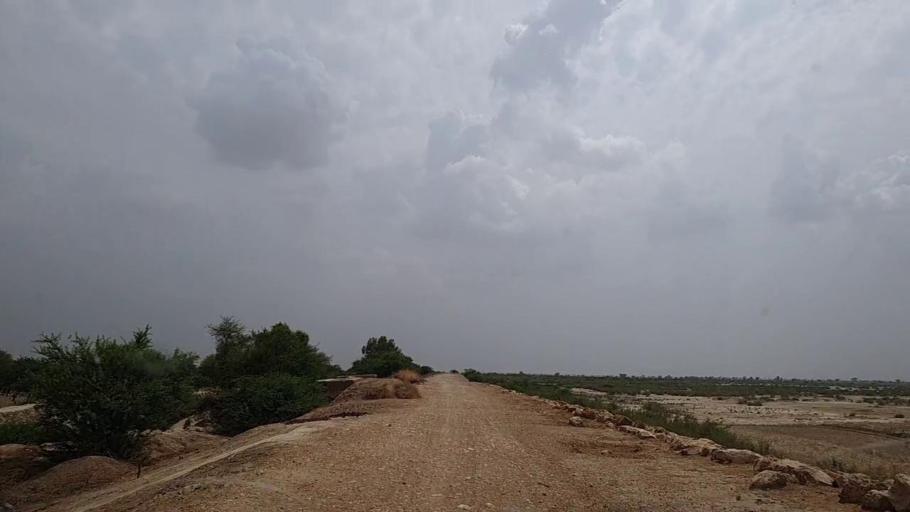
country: PK
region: Sindh
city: Johi
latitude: 26.7359
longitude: 67.5817
